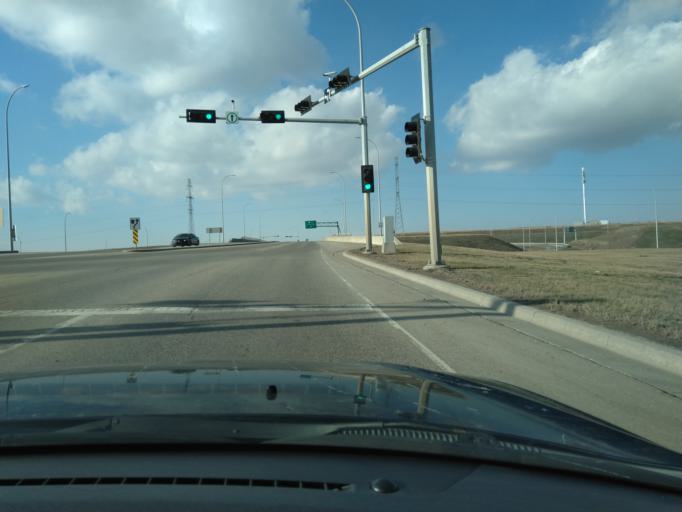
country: CA
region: Alberta
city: Calgary
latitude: 51.1719
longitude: -114.0687
